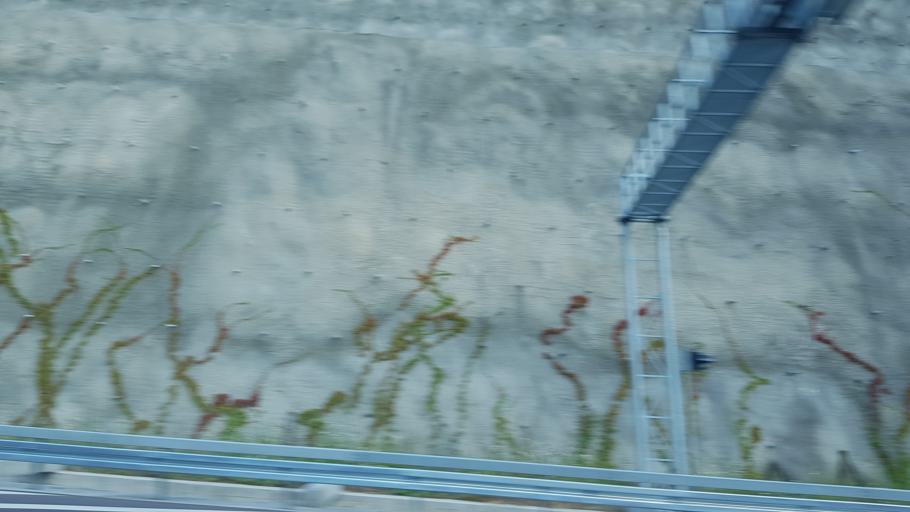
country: TR
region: Bursa
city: Yenikoy
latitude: 40.5843
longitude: 29.3626
